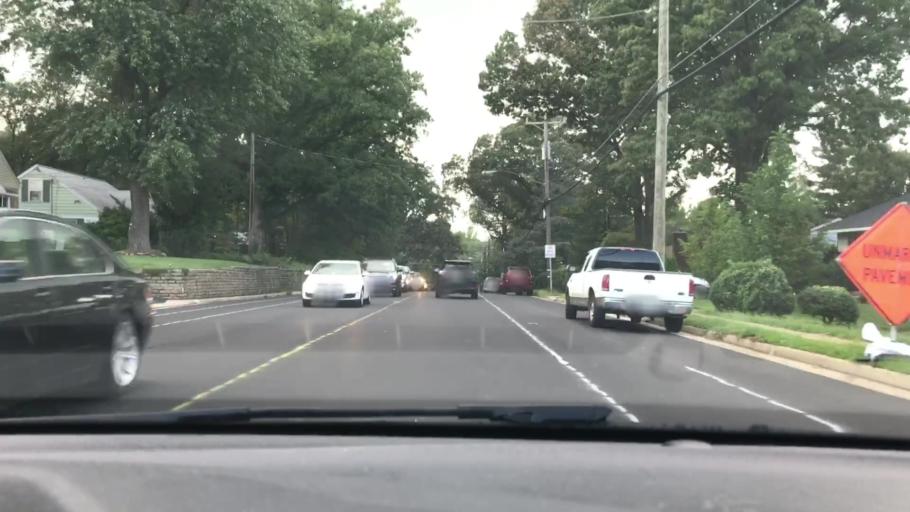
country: US
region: Virginia
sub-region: Fairfax County
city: Annandale
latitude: 38.8351
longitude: -77.1875
